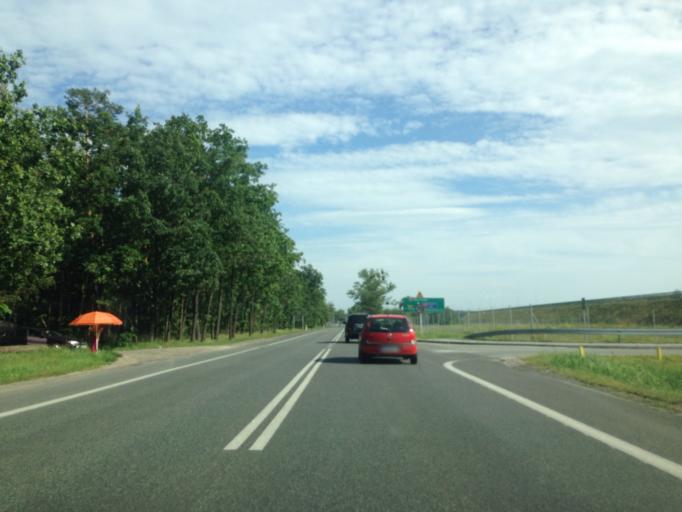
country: PL
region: Kujawsko-Pomorskie
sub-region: Powiat aleksandrowski
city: Ciechocinek
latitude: 52.8748
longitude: 18.7507
